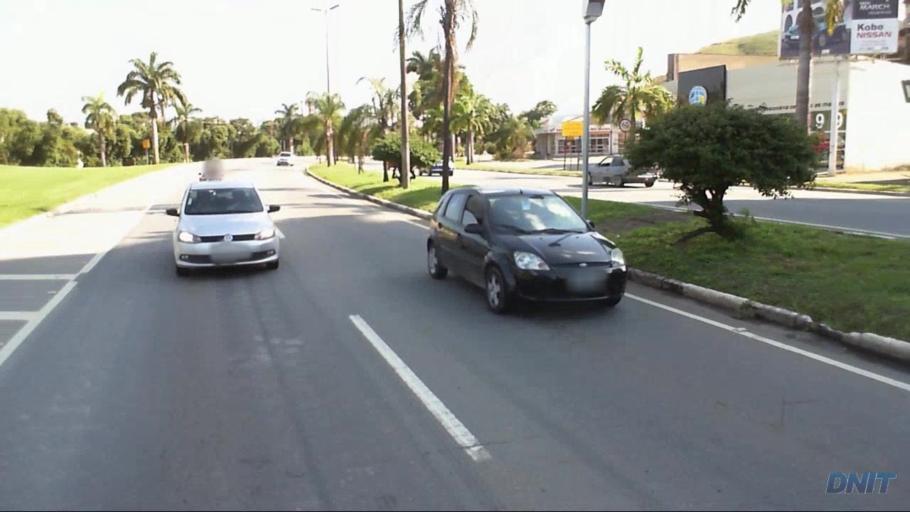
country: BR
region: Minas Gerais
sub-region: Ipatinga
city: Ipatinga
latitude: -19.4804
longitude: -42.5450
